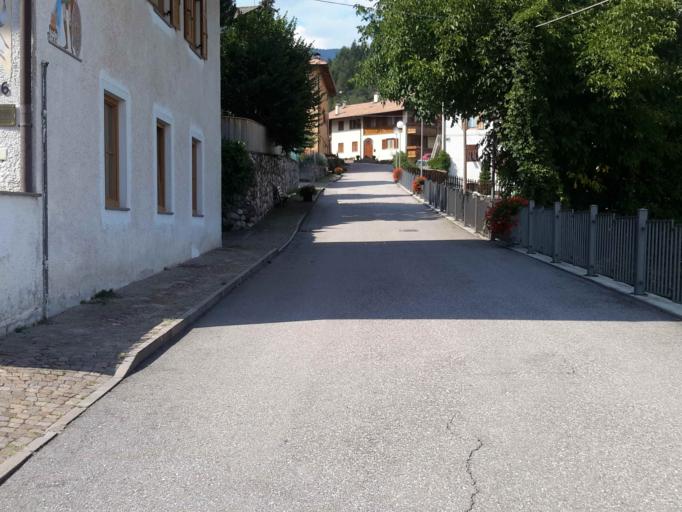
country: IT
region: Trentino-Alto Adige
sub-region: Provincia di Trento
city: Castelfondo
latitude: 46.4546
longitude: 11.1081
